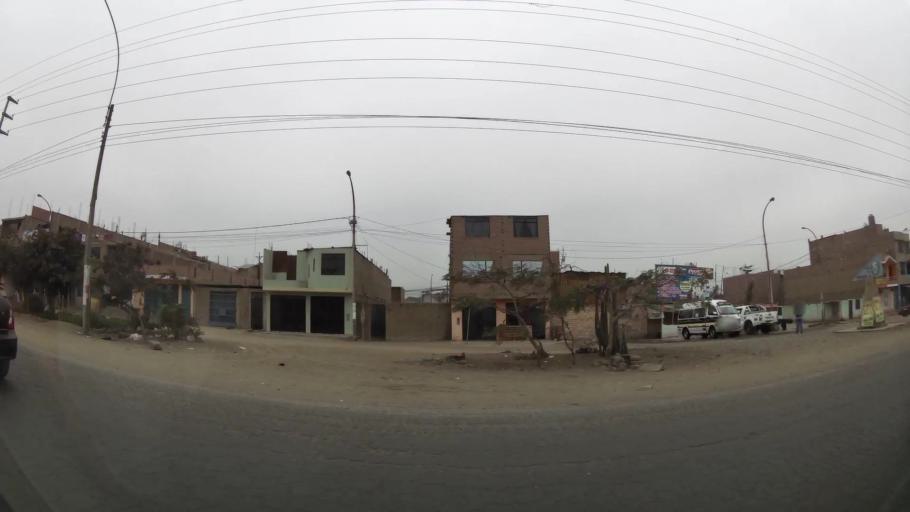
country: PE
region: Lima
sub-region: Lima
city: Urb. Santo Domingo
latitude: -11.8986
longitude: -77.0493
